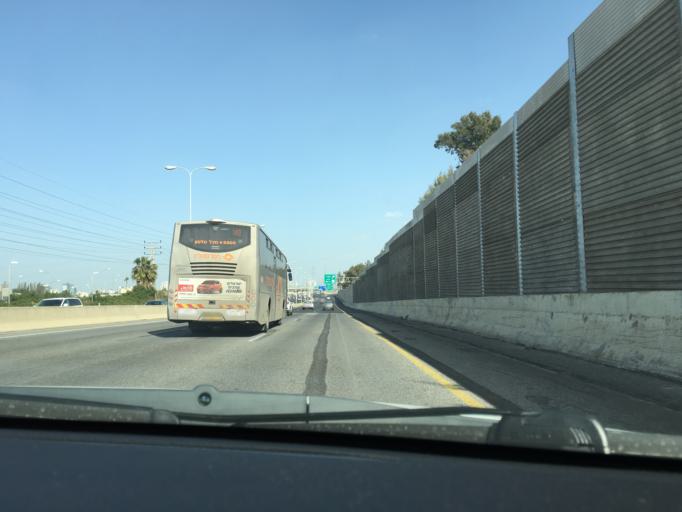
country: IL
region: Central District
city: Hod HaSharon
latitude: 32.1661
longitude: 34.8807
